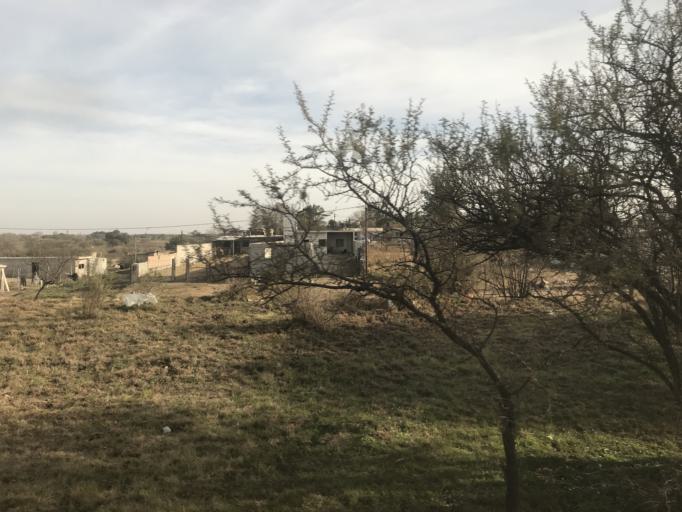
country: AR
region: Cordoba
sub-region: Departamento de Rio Segundo
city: Rio Segundo
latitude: -31.6610
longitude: -63.9040
